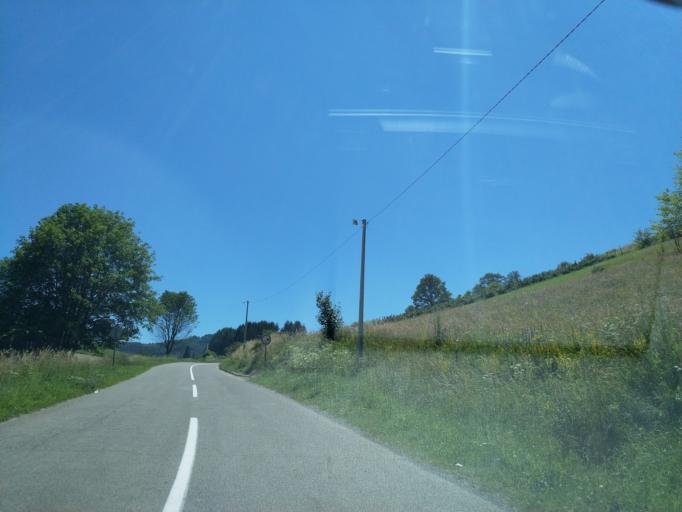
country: XK
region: Mitrovica
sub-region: Komuna e Leposaviqit
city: Leposaviq
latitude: 43.2822
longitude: 20.8750
